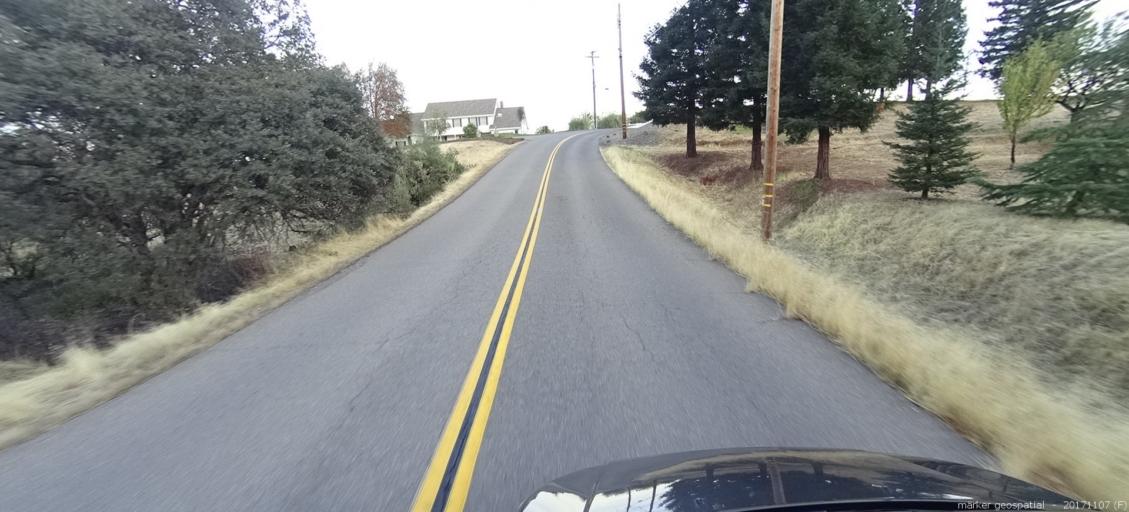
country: US
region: California
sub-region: Shasta County
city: Shasta
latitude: 40.5417
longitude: -122.4775
